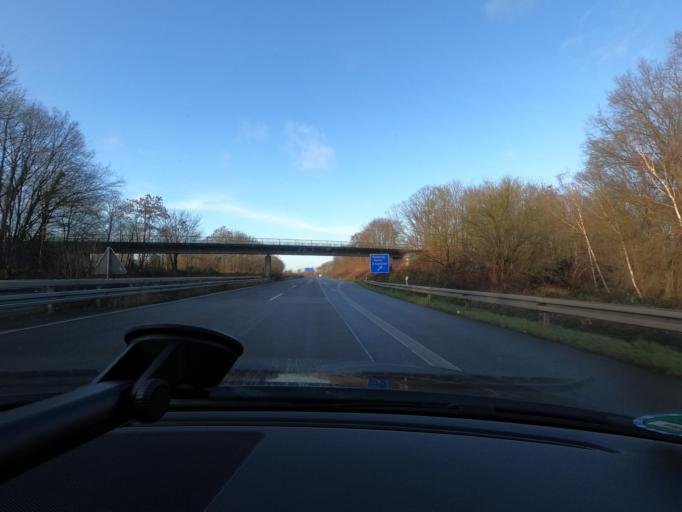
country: DE
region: North Rhine-Westphalia
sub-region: Regierungsbezirk Dusseldorf
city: Ratingen
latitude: 51.3521
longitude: 6.7945
